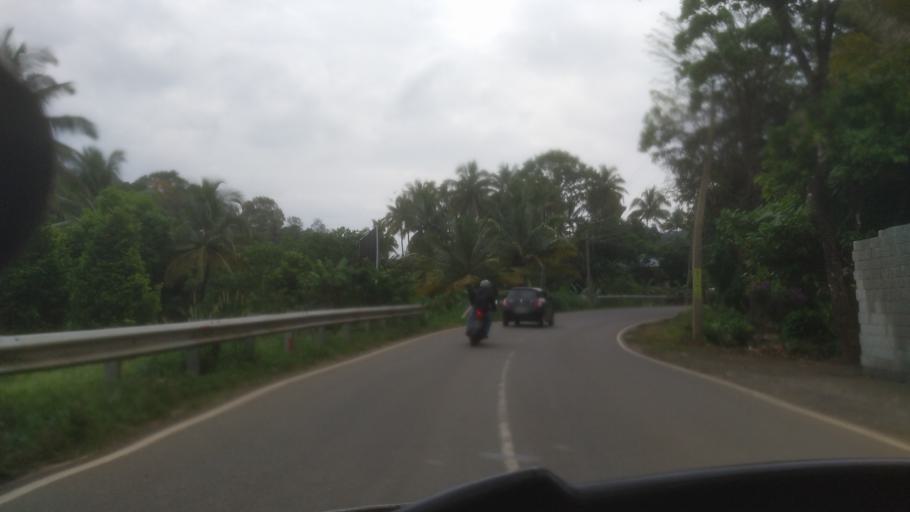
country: IN
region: Kerala
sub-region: Idukki
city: Munnar
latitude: 9.9903
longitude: 76.9829
